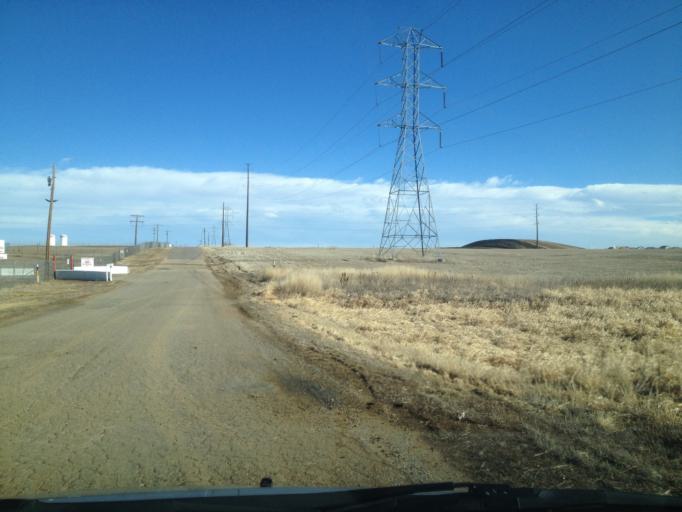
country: US
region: Colorado
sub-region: Weld County
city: Dacono
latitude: 40.0585
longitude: -104.9749
